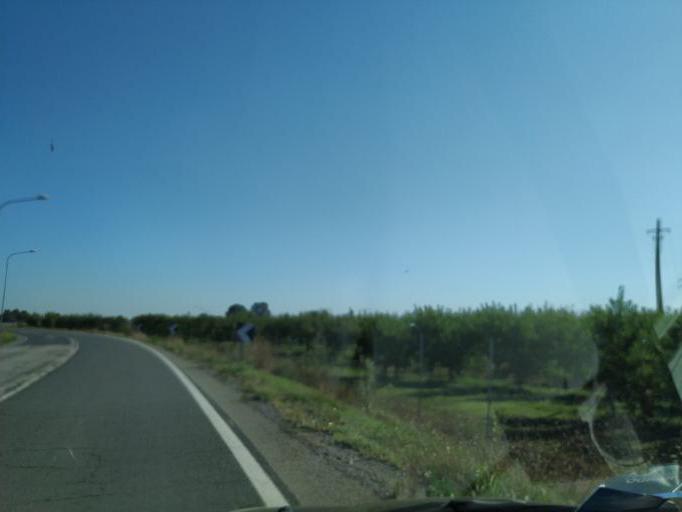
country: IT
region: Emilia-Romagna
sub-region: Provincia di Bologna
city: Decima
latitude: 44.6989
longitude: 11.2351
